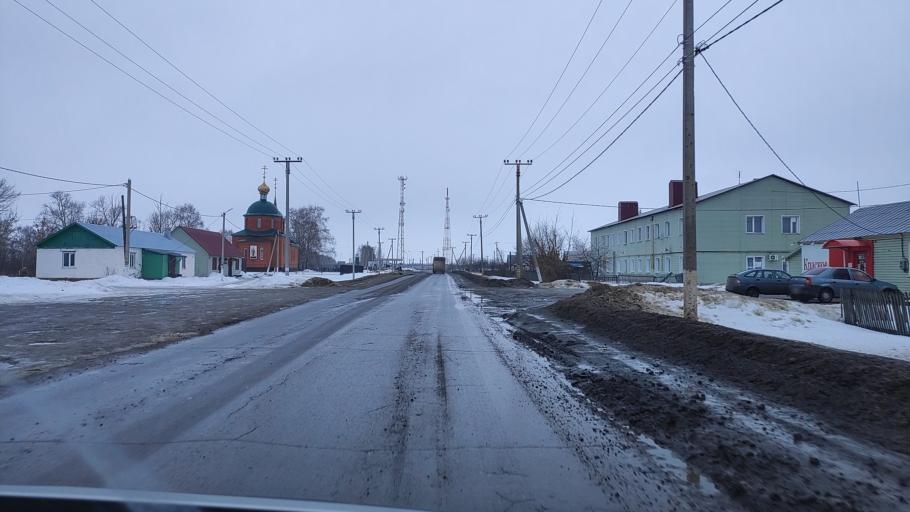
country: RU
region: Tambov
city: Novopokrovka
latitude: 51.9919
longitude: 41.1537
